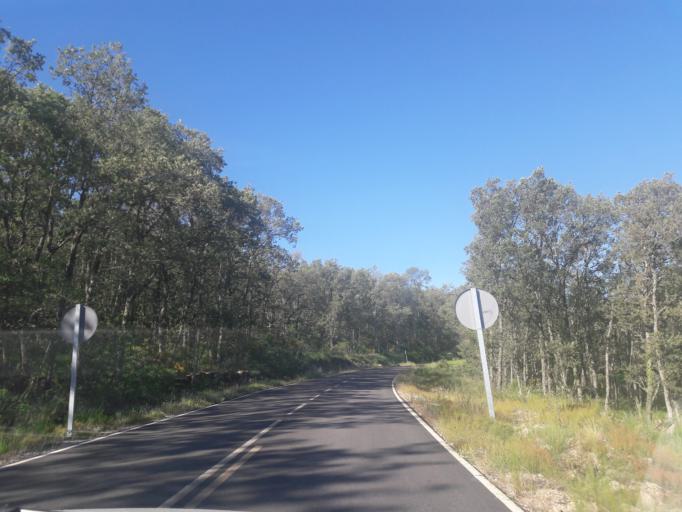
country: ES
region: Castille and Leon
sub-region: Provincia de Salamanca
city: Montemayor del Rio
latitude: 40.3377
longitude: -5.8902
